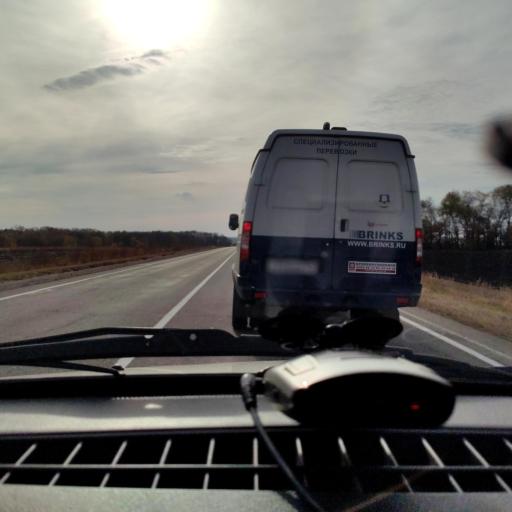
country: RU
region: Voronezj
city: Shilovo
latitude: 51.4611
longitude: 38.9699
